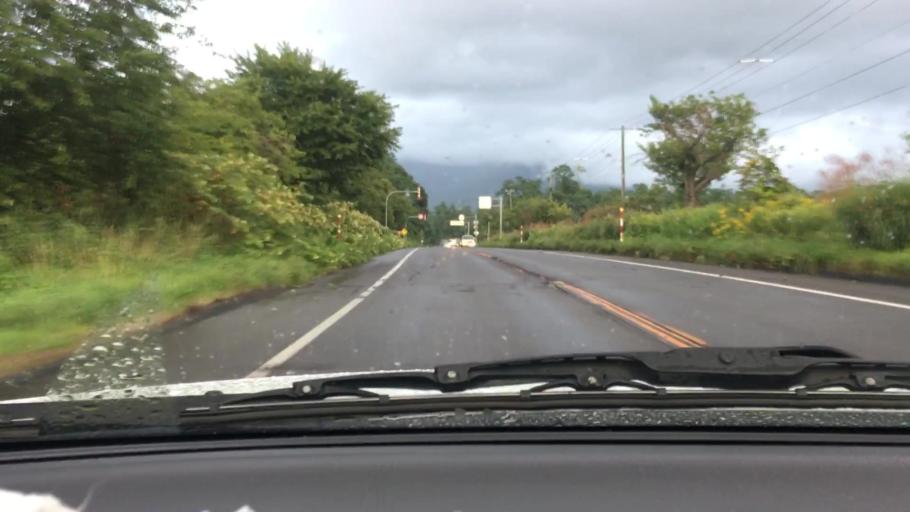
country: JP
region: Hokkaido
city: Nanae
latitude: 42.0809
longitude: 140.5912
